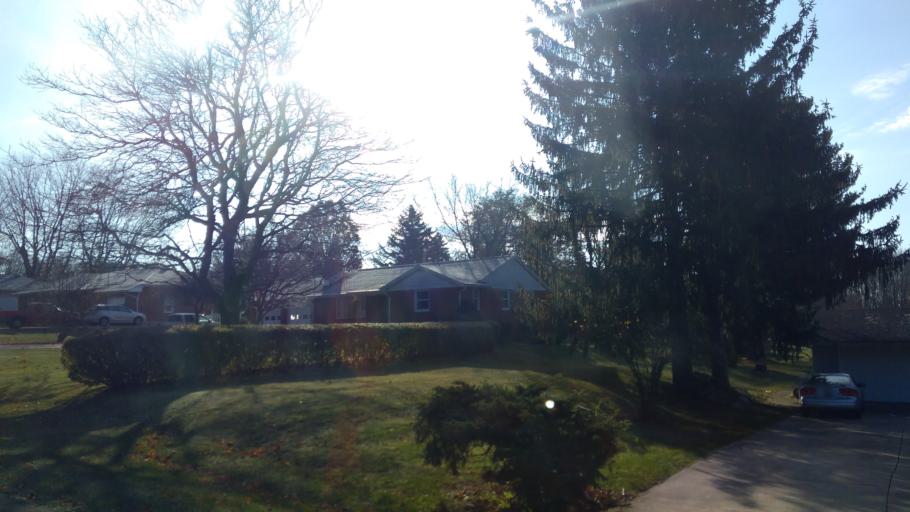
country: US
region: Ohio
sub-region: Richland County
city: Lexington
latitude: 40.6973
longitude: -82.5447
